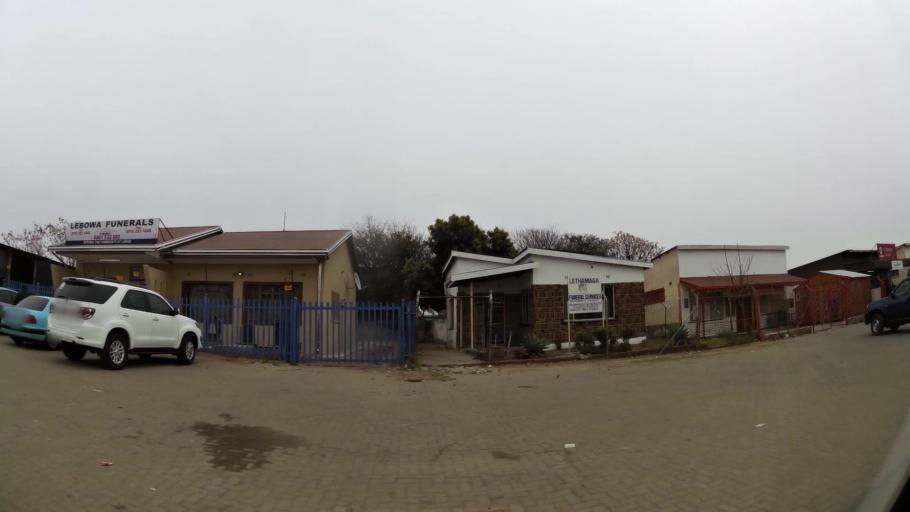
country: ZA
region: Limpopo
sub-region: Capricorn District Municipality
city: Polokwane
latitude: -23.8473
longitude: 29.3913
